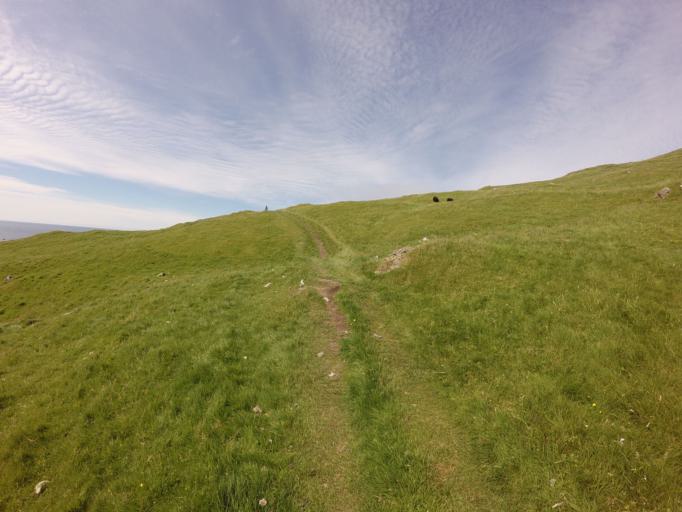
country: FO
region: Vagar
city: Sorvagur
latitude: 62.1003
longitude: -7.6660
